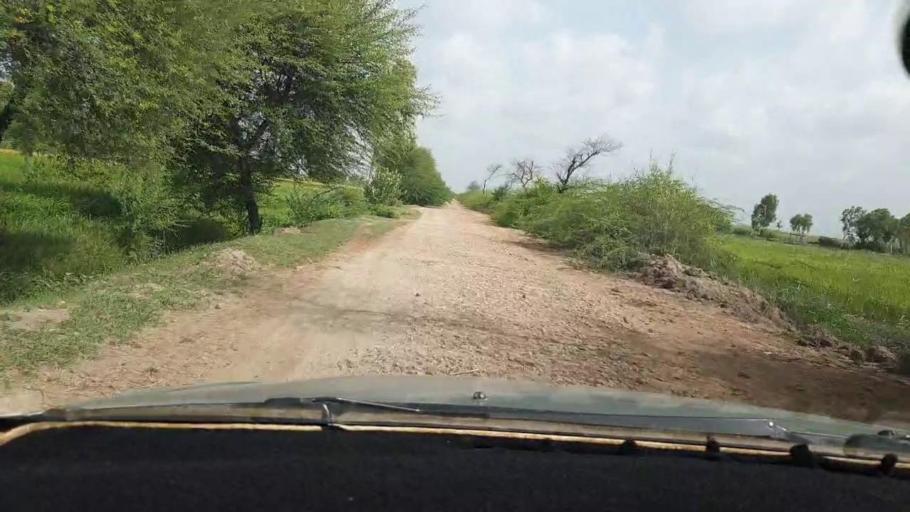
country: PK
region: Sindh
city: Tando Bago
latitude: 24.7752
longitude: 69.0250
